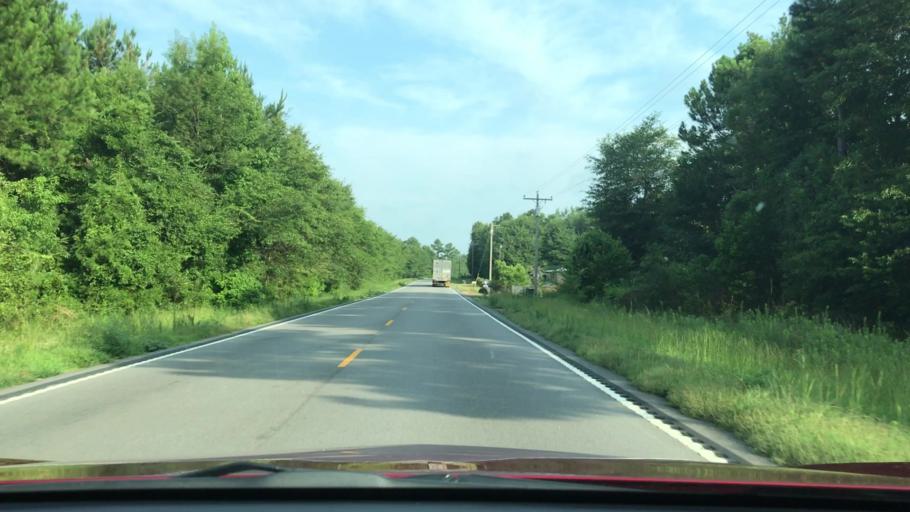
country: US
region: South Carolina
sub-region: Barnwell County
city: Blackville
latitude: 33.5502
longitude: -81.1571
